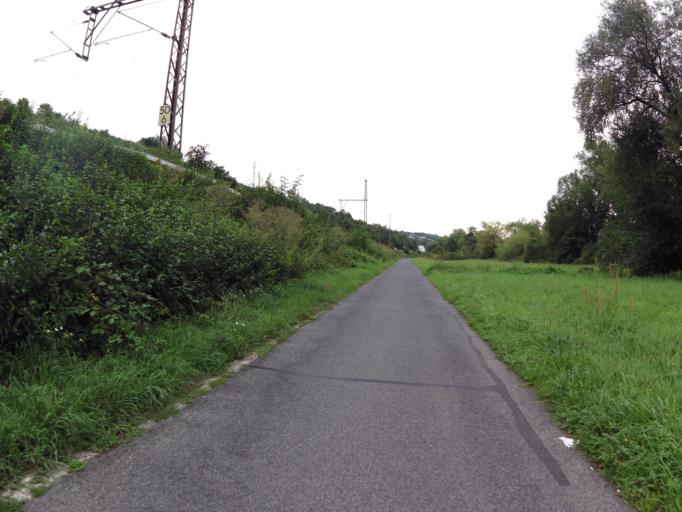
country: DE
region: Bavaria
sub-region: Regierungsbezirk Unterfranken
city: Schonungen
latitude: 50.0557
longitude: 10.2899
